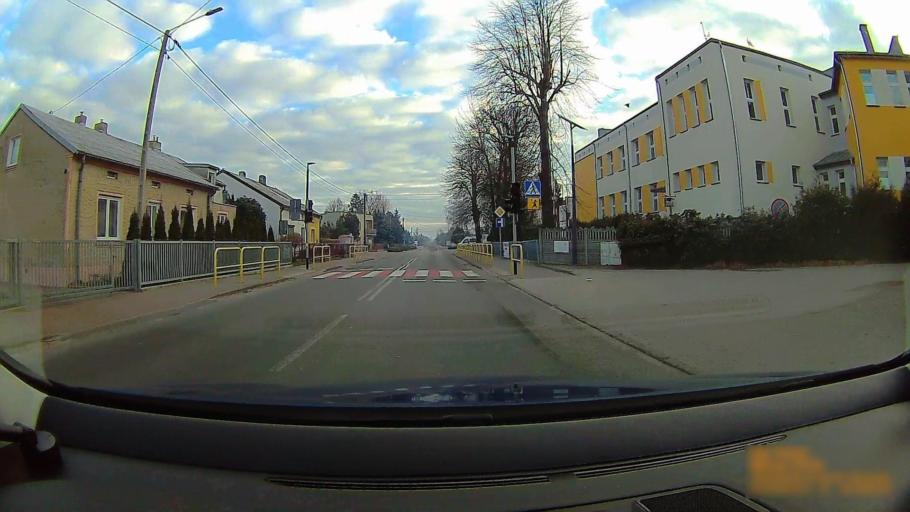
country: PL
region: Greater Poland Voivodeship
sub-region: Powiat koninski
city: Rzgow Pierwszy
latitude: 52.1541
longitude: 18.0519
